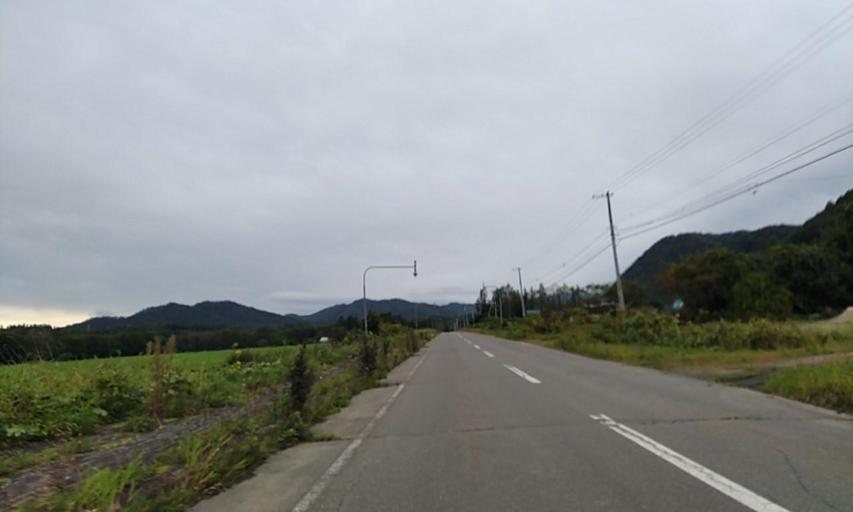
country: JP
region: Hokkaido
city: Obihiro
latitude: 42.6858
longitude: 143.0487
